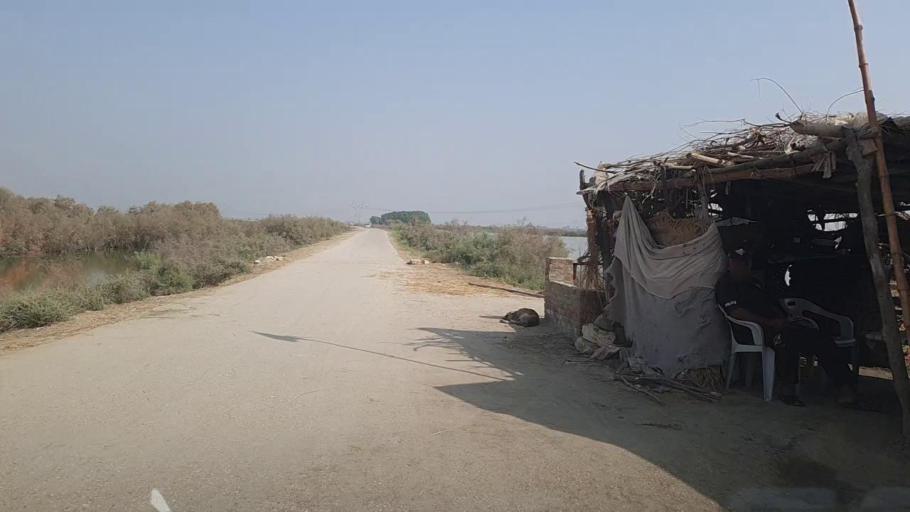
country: PK
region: Sindh
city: Kandhkot
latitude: 28.2252
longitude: 69.1872
